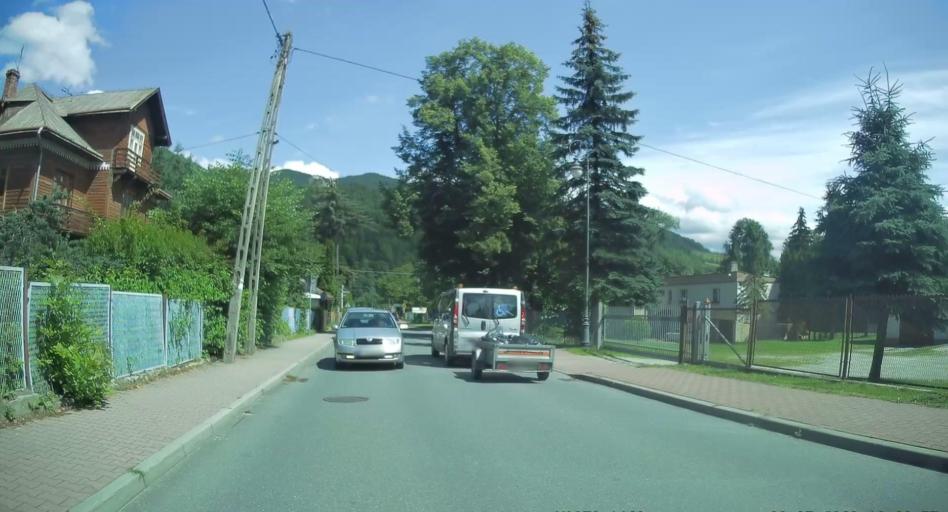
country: PL
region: Lesser Poland Voivodeship
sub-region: Powiat nowosadecki
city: Rytro
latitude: 49.4897
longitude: 20.6790
